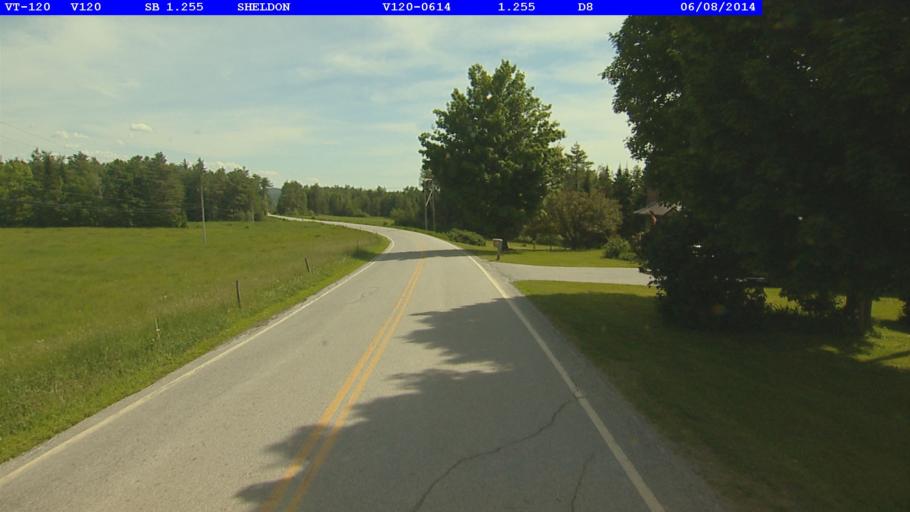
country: US
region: Vermont
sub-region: Franklin County
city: Enosburg Falls
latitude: 44.9280
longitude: -72.9023
